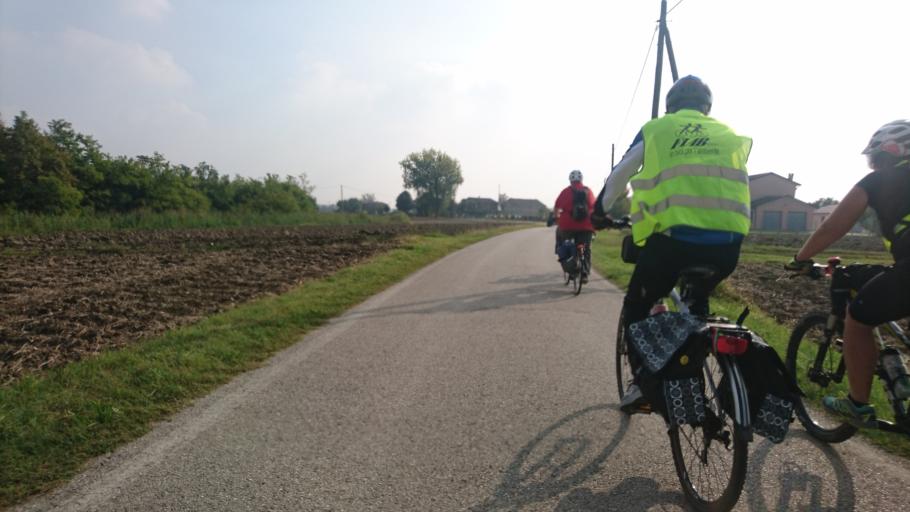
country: IT
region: Veneto
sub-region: Provincia di Rovigo
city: Bosaro
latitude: 44.9867
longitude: 11.7513
